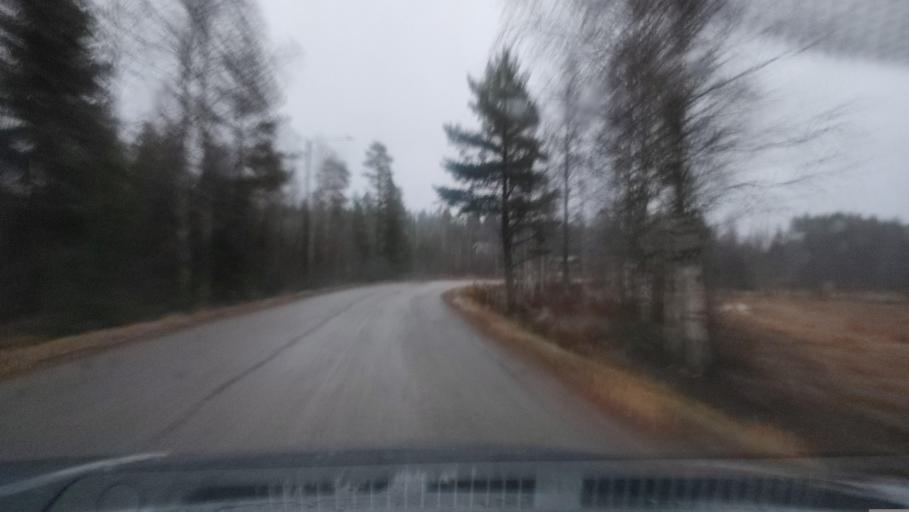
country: FI
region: Southern Ostrobothnia
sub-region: Suupohja
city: Karijoki
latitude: 62.1448
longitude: 21.5657
